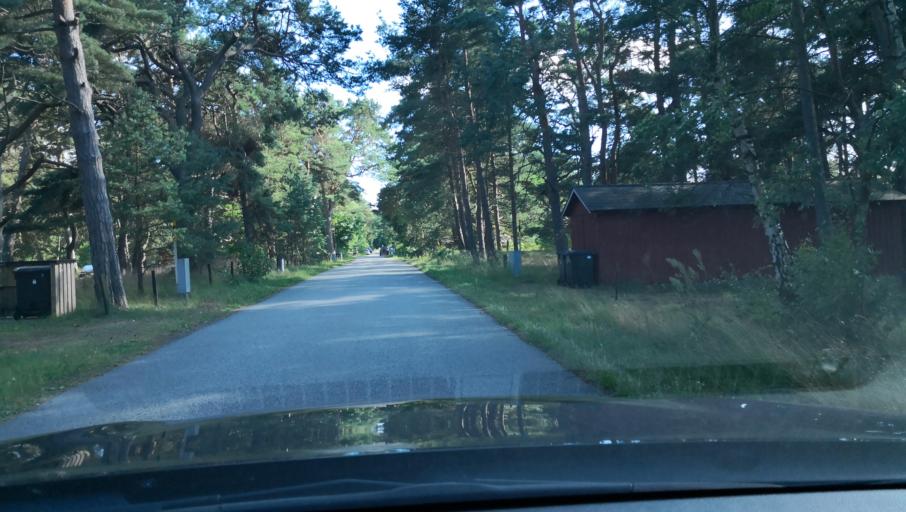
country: SE
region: Skane
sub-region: Simrishamns Kommun
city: Kivik
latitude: 55.7695
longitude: 14.1958
